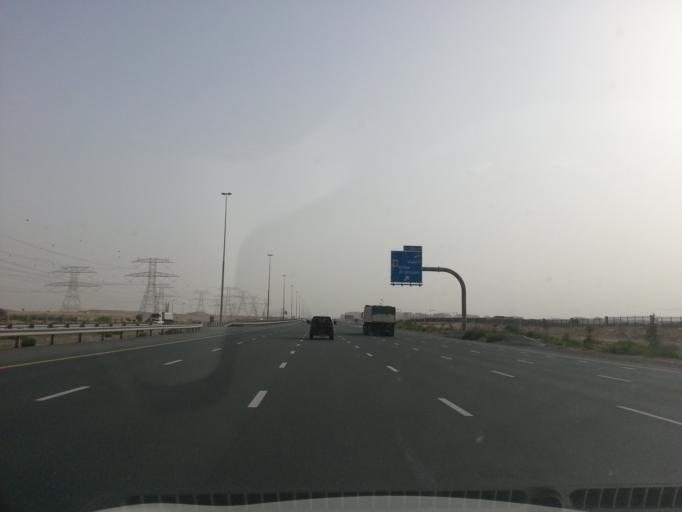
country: AE
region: Dubai
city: Dubai
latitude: 25.0136
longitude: 55.2710
